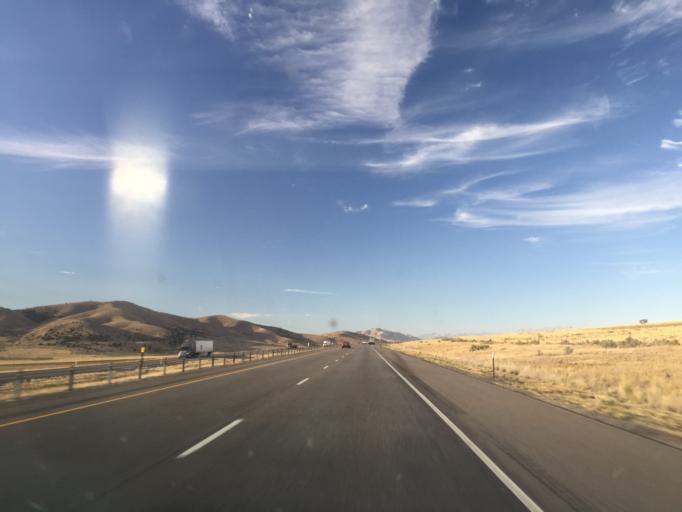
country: US
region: Utah
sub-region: Juab County
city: Mona
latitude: 39.8889
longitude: -111.8282
